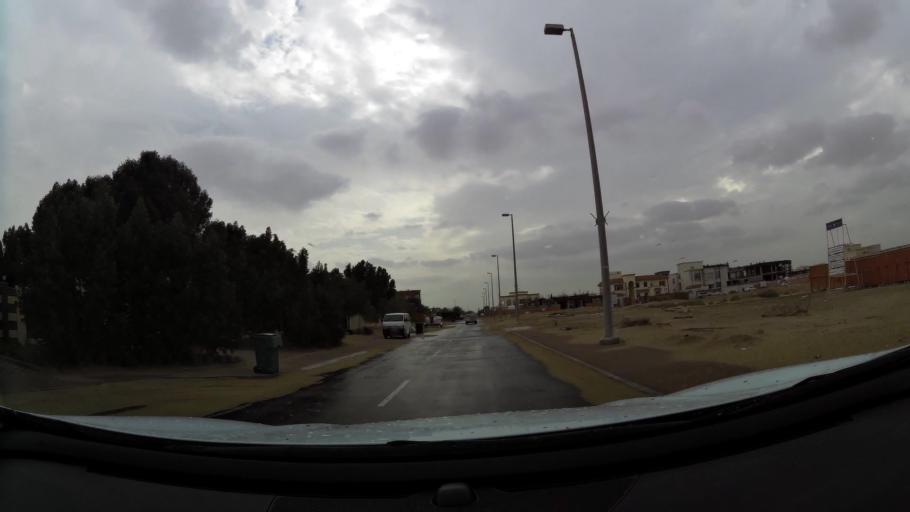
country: AE
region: Abu Dhabi
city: Abu Dhabi
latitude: 24.3643
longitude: 54.6248
